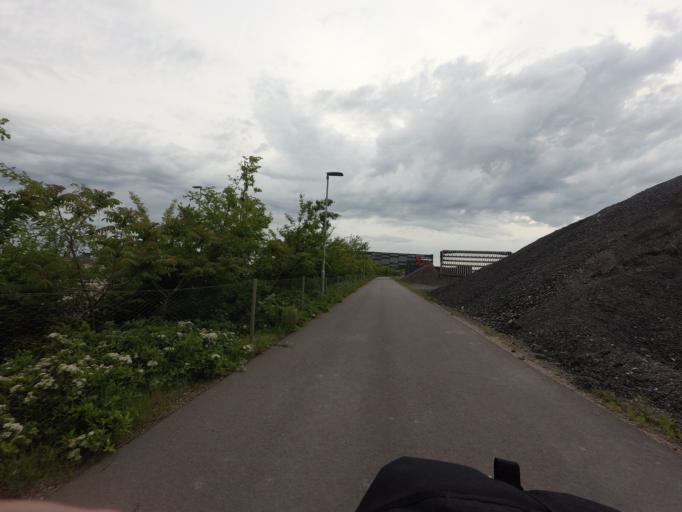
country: SE
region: Skane
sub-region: Malmo
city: Malmoe
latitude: 55.6312
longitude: 13.0093
